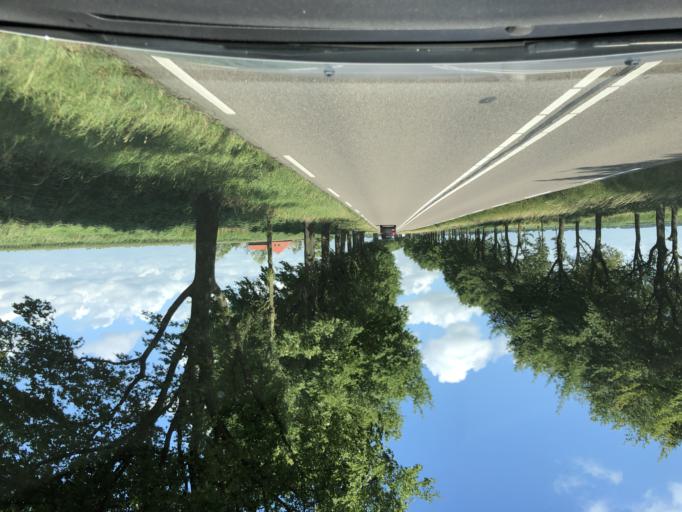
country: NL
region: North Holland
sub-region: Gemeente Edam-Volendam
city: Edam
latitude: 52.5469
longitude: 5.0216
